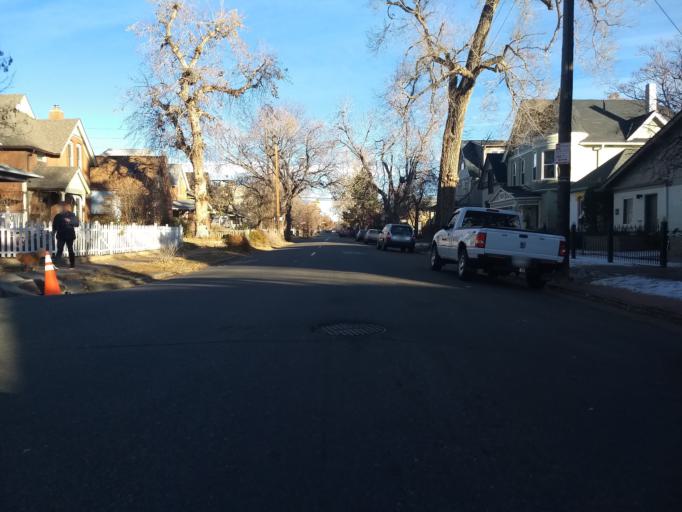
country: US
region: Colorado
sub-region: Denver County
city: Denver
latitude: 39.7166
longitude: -104.9909
